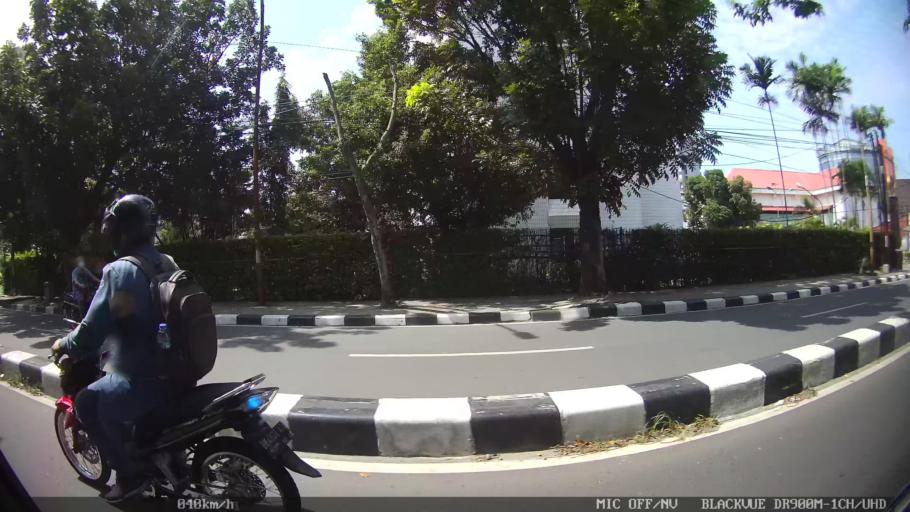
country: ID
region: North Sumatra
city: Medan
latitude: 3.5842
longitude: 98.6761
